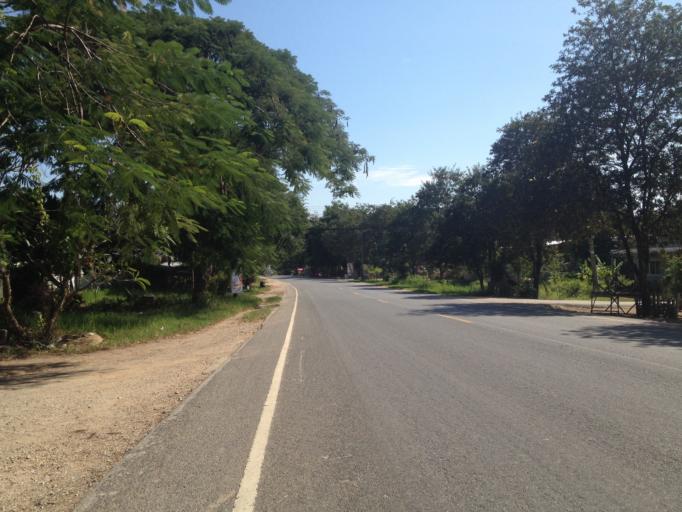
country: TH
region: Chiang Mai
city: Hang Dong
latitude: 18.7548
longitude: 98.8864
